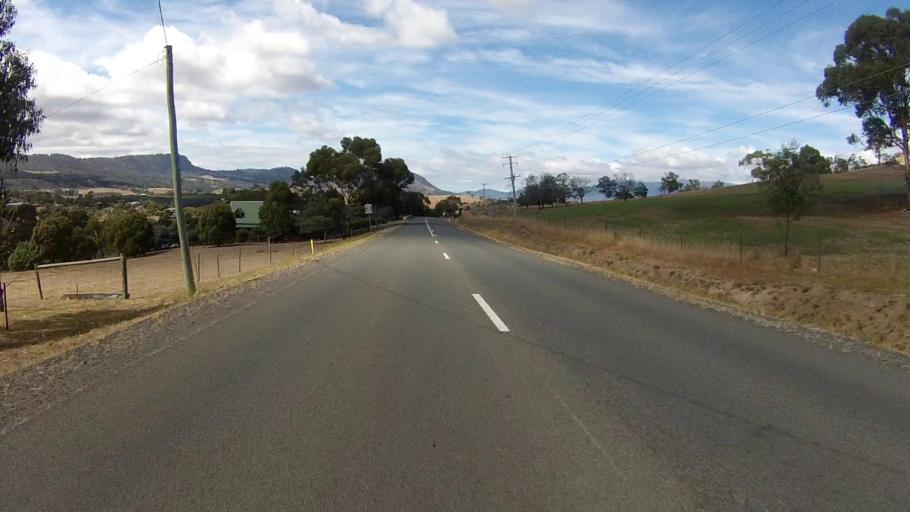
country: AU
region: Tasmania
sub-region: Brighton
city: Old Beach
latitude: -42.7320
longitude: 147.2889
